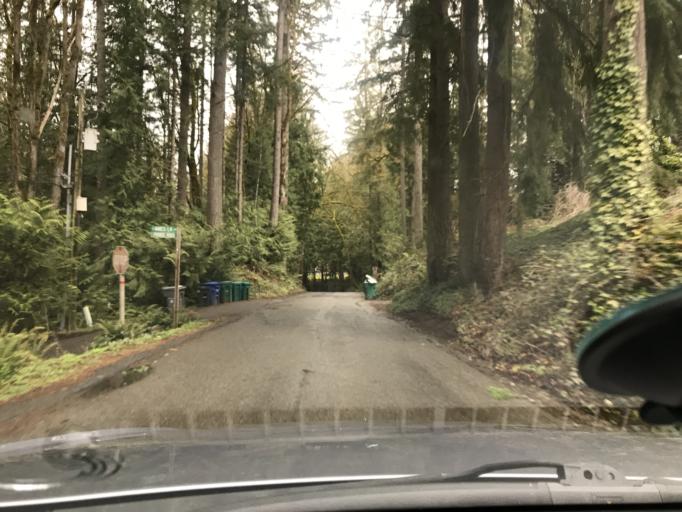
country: US
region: Washington
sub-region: King County
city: Ames Lake
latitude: 47.6439
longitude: -121.9542
